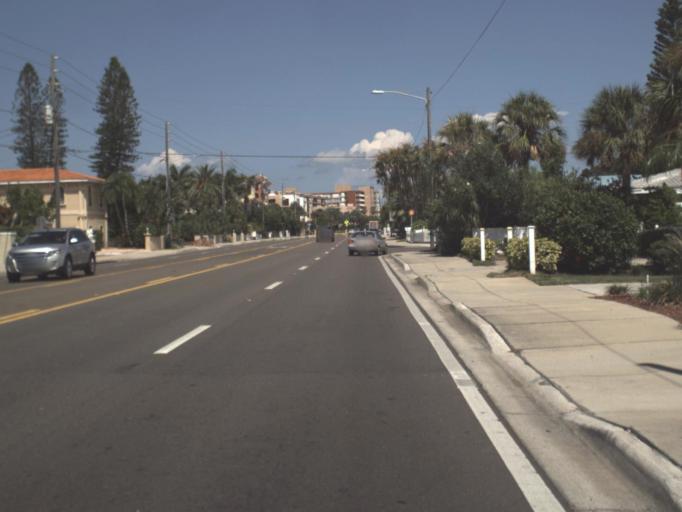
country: US
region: Florida
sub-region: Pinellas County
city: Redington Beach
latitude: 27.8110
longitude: -82.8149
